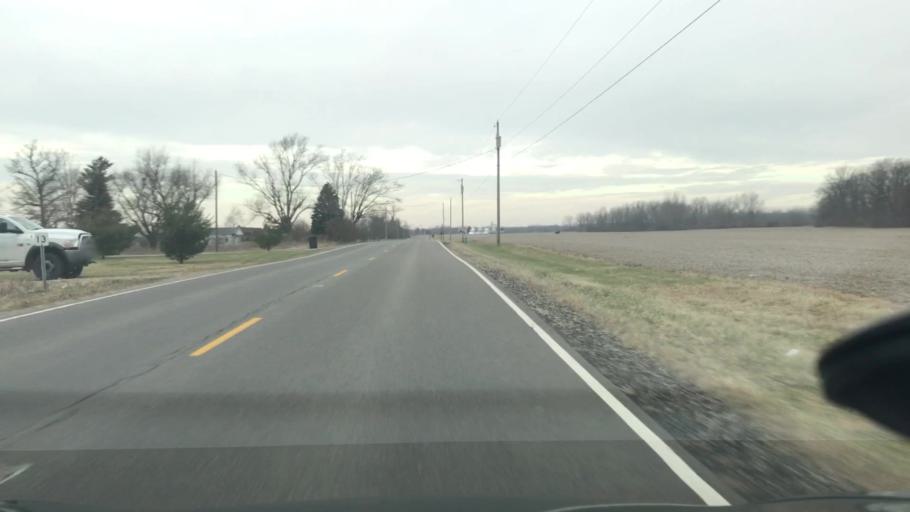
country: US
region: Ohio
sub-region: Madison County
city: London
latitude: 39.8368
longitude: -83.3786
